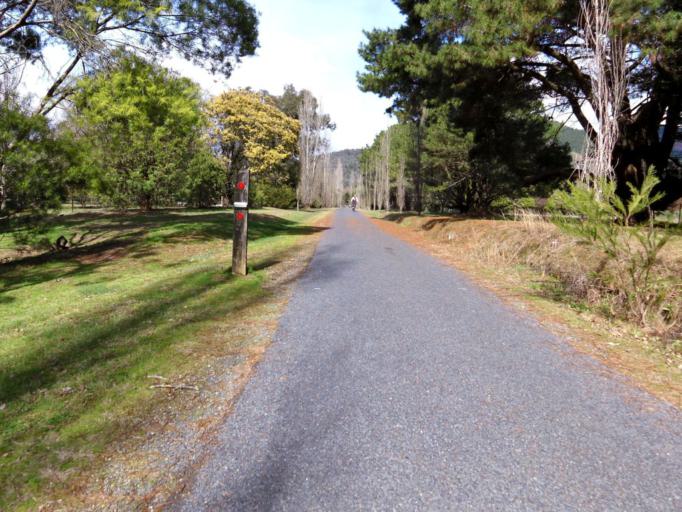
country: AU
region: Victoria
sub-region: Alpine
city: Mount Beauty
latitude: -36.7207
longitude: 146.9451
